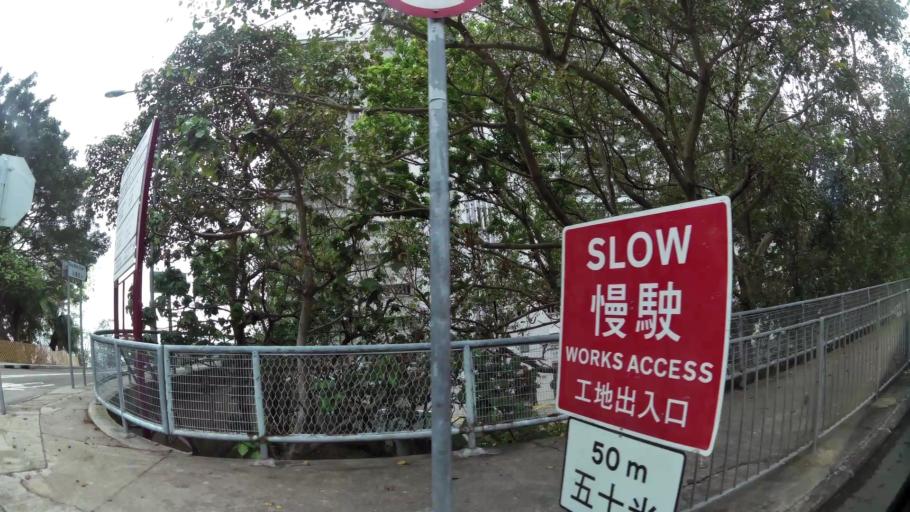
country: HK
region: Central and Western
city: Central
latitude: 22.2682
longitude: 114.1270
